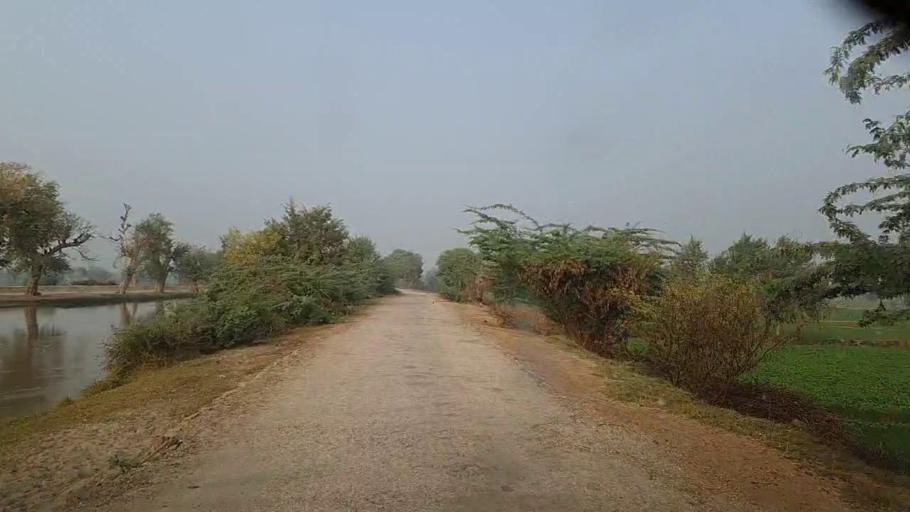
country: PK
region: Sindh
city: Bozdar
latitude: 27.1602
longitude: 68.6605
